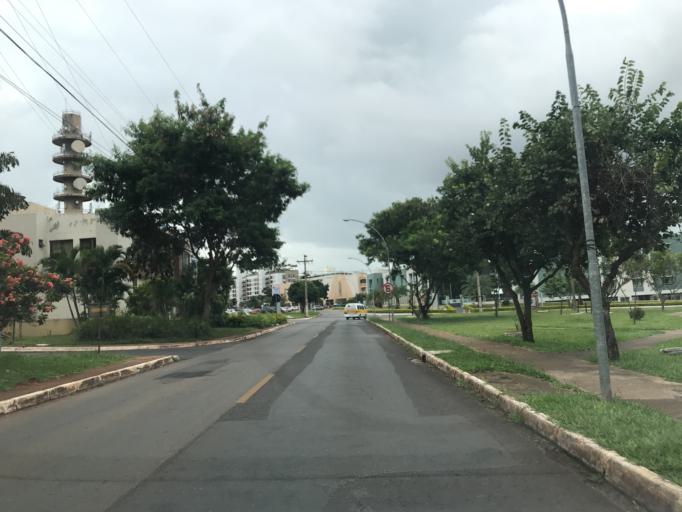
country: BR
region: Federal District
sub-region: Brasilia
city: Brasilia
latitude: -15.7947
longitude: -47.9215
